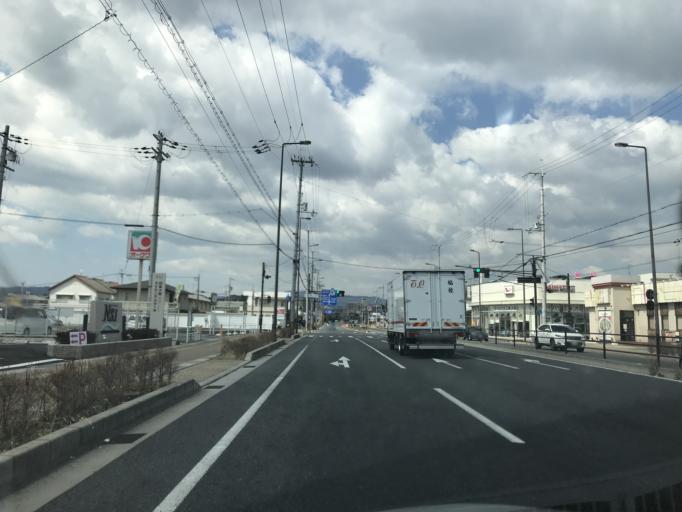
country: JP
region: Nara
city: Nara-shi
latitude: 34.6818
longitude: 135.7923
